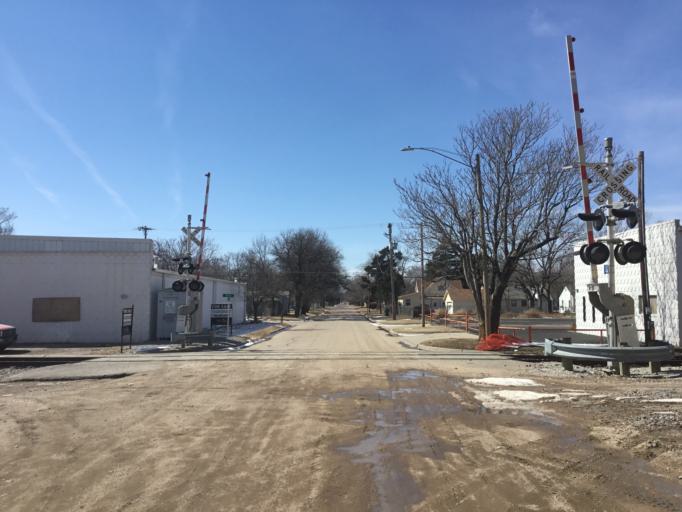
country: US
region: Kansas
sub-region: Sedgwick County
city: Wichita
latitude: 37.6607
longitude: -97.3288
